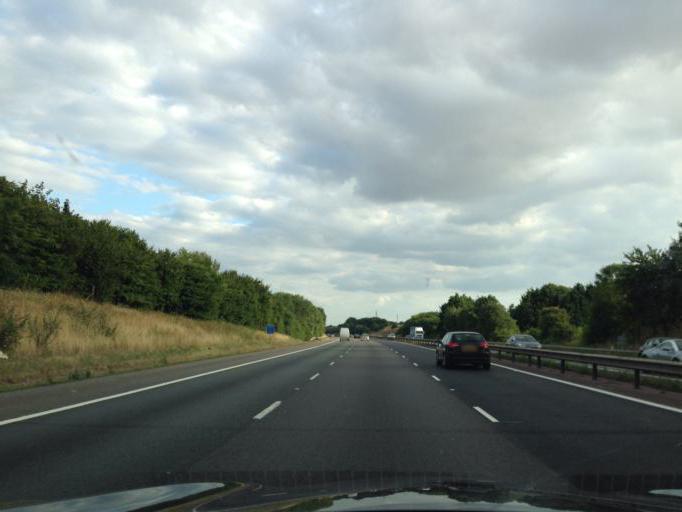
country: GB
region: England
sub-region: Oxfordshire
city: Adderbury
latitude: 52.0367
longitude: -1.3032
